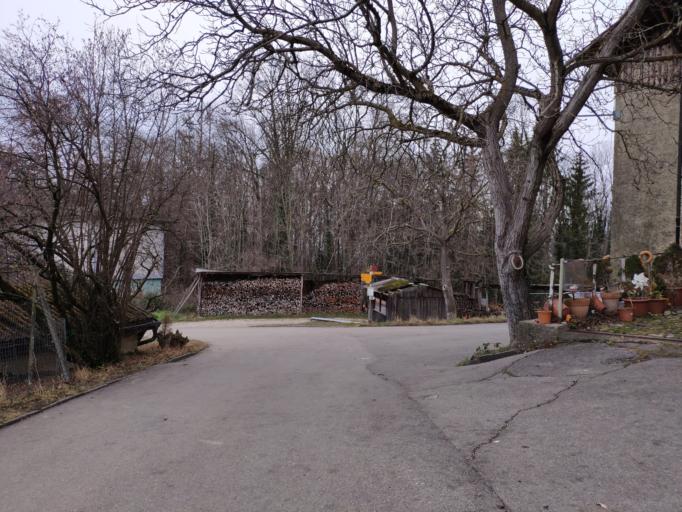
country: CH
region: Basel-City
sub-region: Basel-Stadt
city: Bettingen
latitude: 47.5730
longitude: 7.6792
